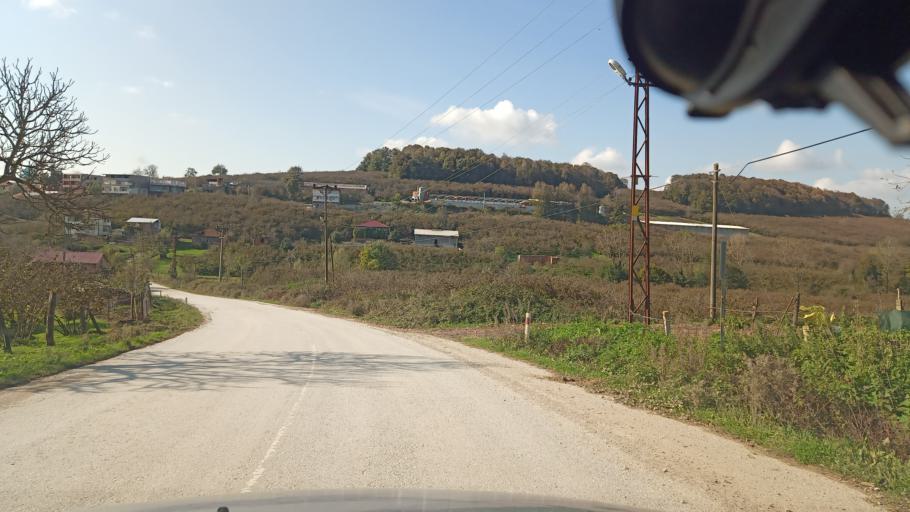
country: TR
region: Sakarya
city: Ferizli
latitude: 41.0953
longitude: 30.4583
